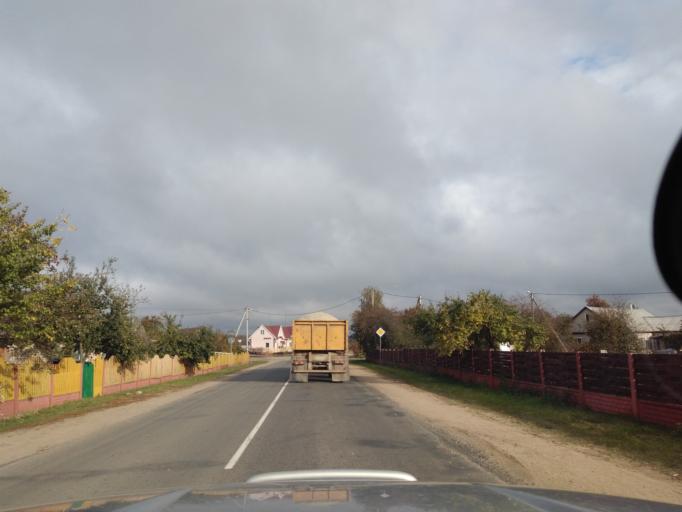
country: BY
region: Minsk
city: Kapyl'
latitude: 53.1514
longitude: 27.0744
